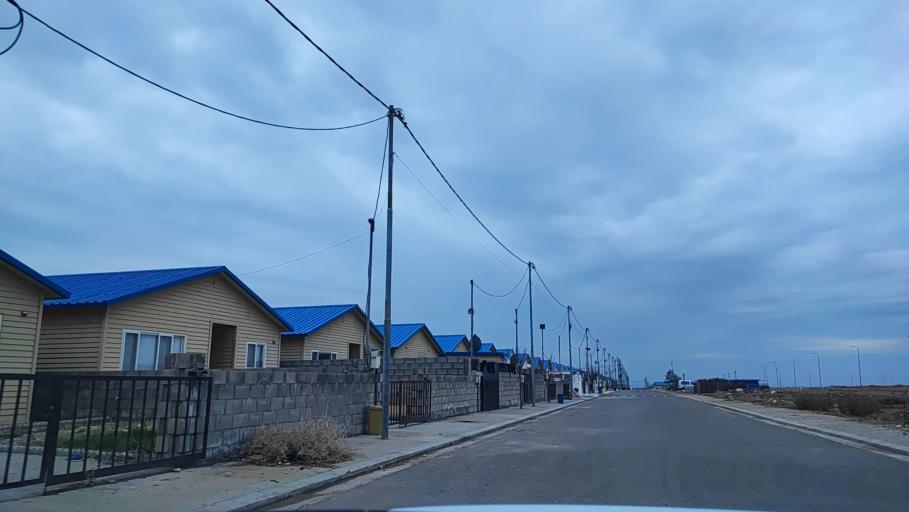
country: IQ
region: Arbil
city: Erbil
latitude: 36.2858
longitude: 44.0836
